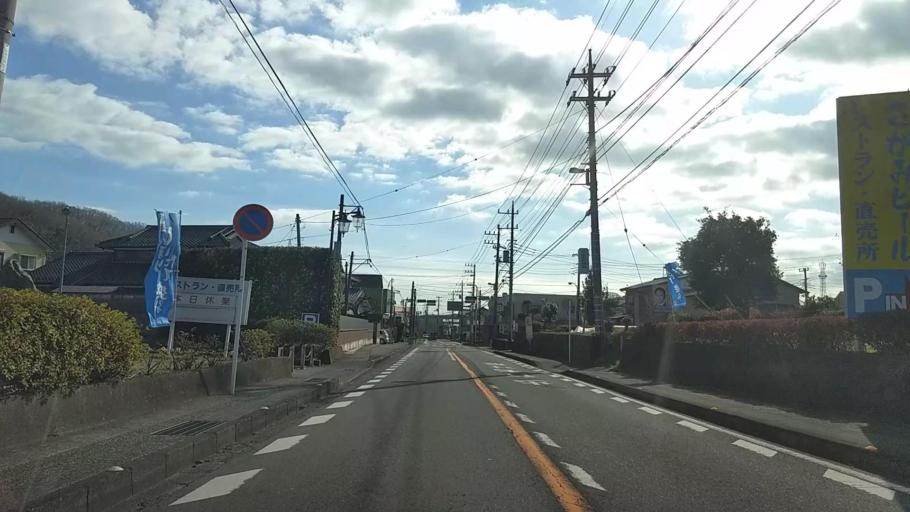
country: JP
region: Kanagawa
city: Isehara
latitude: 35.4431
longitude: 139.2987
